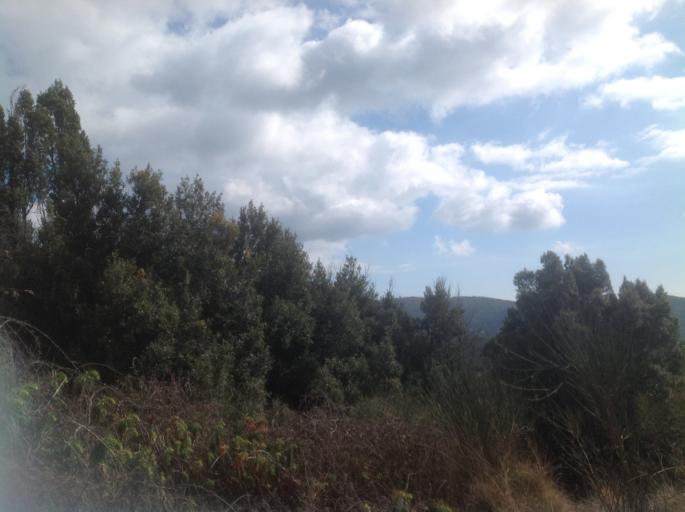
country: IT
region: Calabria
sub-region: Provincia di Cosenza
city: Civita
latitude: 39.8467
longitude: 16.3052
